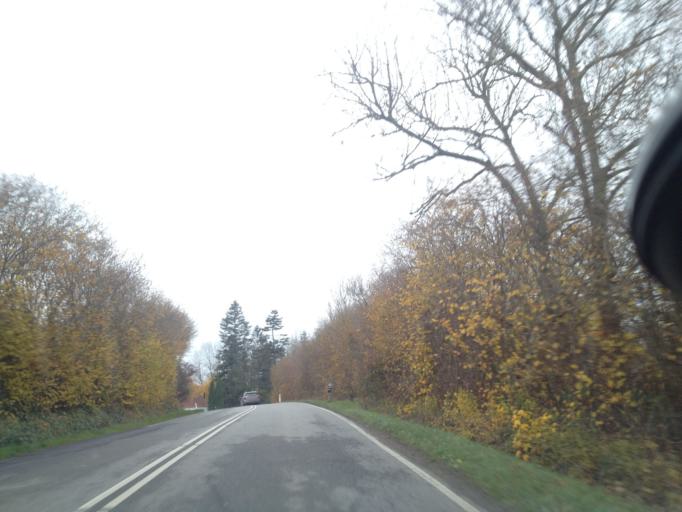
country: DK
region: South Denmark
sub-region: Assens Kommune
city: Vissenbjerg
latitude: 55.4479
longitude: 10.1270
